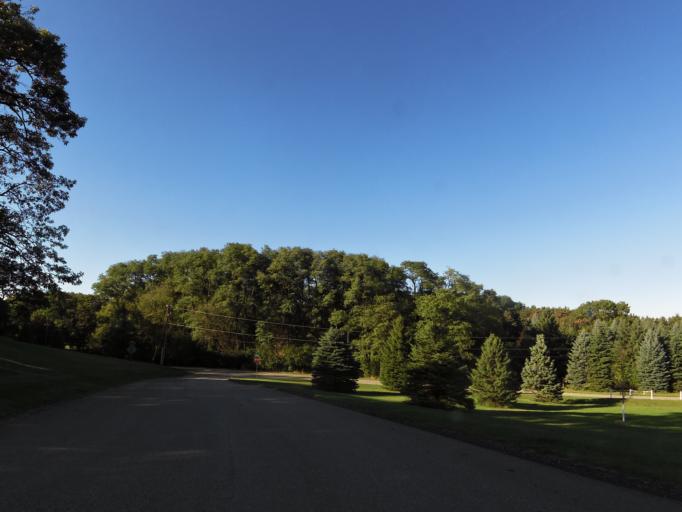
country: US
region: Minnesota
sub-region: Washington County
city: Bayport
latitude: 44.9937
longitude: -92.7957
